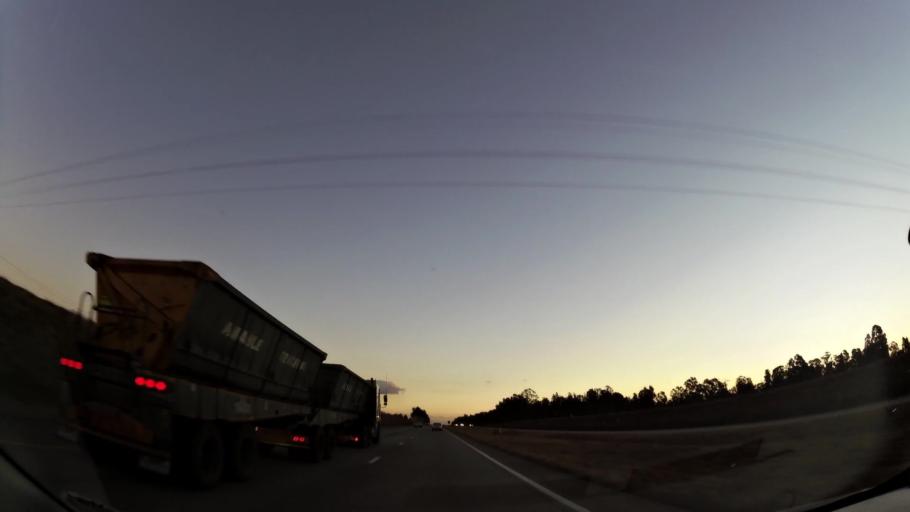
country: ZA
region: Mpumalanga
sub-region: Nkangala District Municipality
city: Witbank
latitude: -25.9723
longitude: 29.1809
